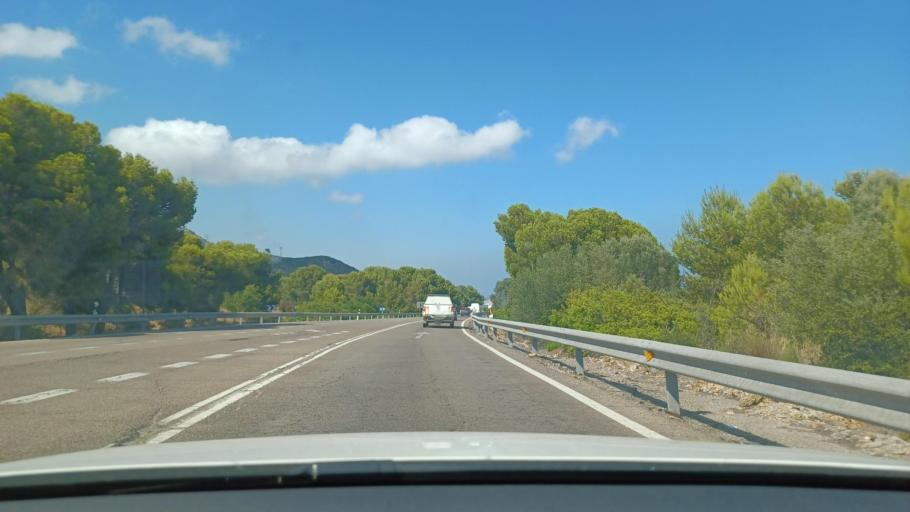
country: ES
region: Valencia
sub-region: Provincia de Castello
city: Orpesa/Oropesa del Mar
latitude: 40.0752
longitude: 0.1113
